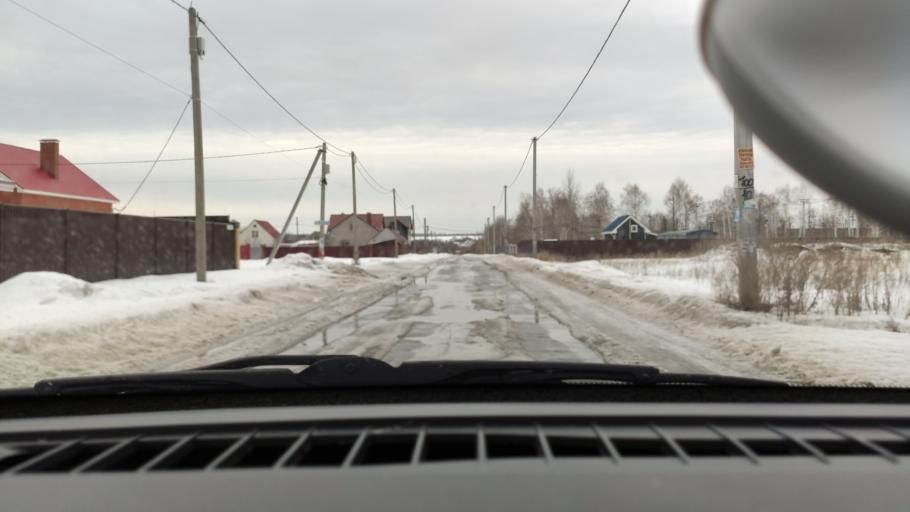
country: RU
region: Samara
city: Kurumoch
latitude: 53.4875
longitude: 50.0185
